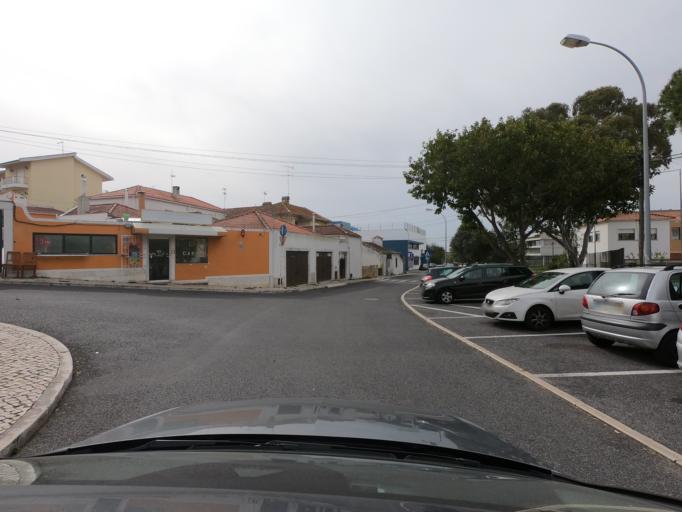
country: PT
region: Lisbon
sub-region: Oeiras
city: Porto Salvo
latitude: 38.7171
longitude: -9.2992
